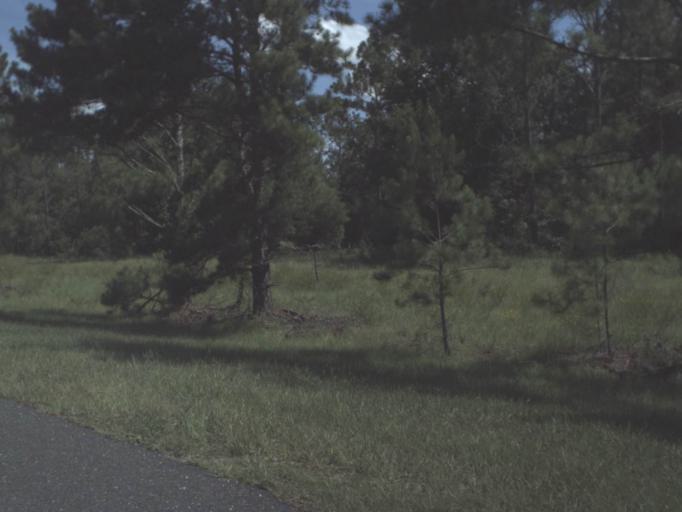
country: US
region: Florida
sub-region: Levy County
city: Chiefland
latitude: 29.4209
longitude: -82.8256
